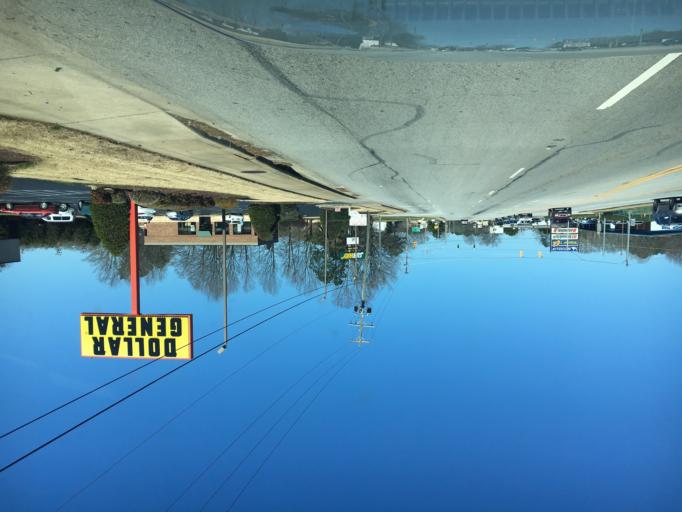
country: US
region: South Carolina
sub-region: Laurens County
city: Clinton
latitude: 34.4528
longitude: -81.8823
